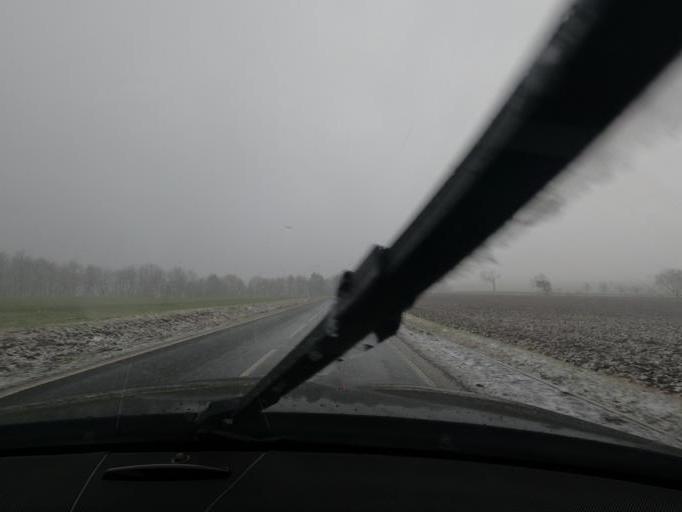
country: DE
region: Thuringia
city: Buttstedt
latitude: 51.2480
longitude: 10.2774
